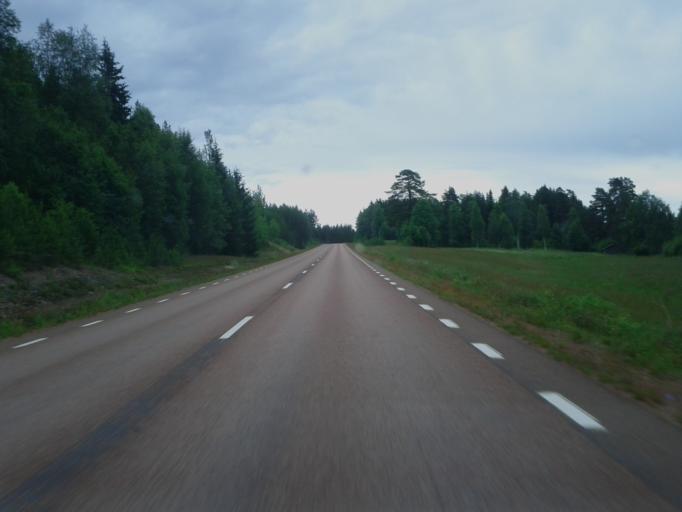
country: SE
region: Dalarna
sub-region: Alvdalens Kommun
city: AElvdalen
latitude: 61.2693
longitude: 14.0019
